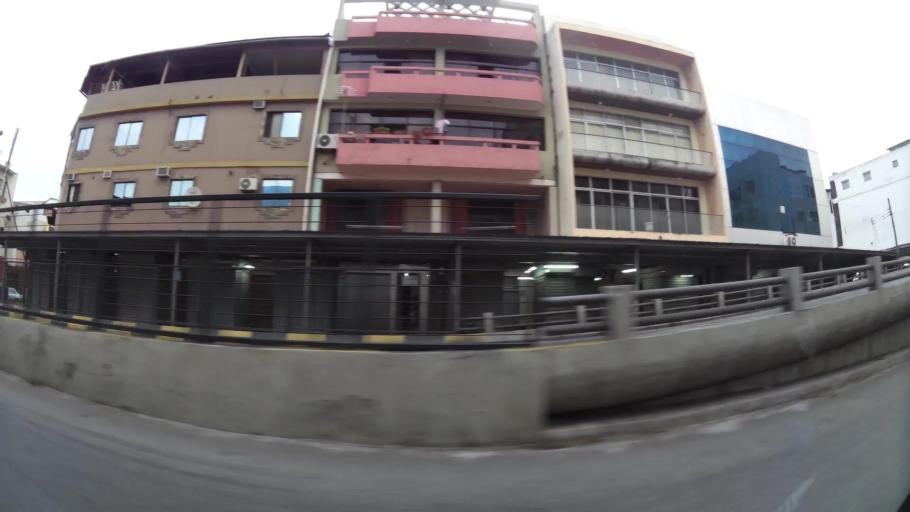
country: EC
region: Guayas
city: Guayaquil
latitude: -2.2020
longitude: -79.8837
